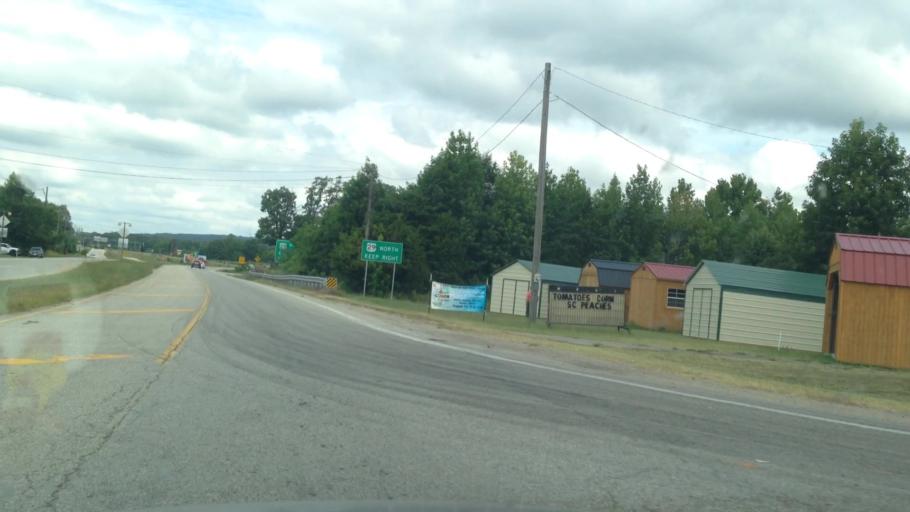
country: US
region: Virginia
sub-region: Pittsylvania County
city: Mount Hermon
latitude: 36.6971
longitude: -79.3668
